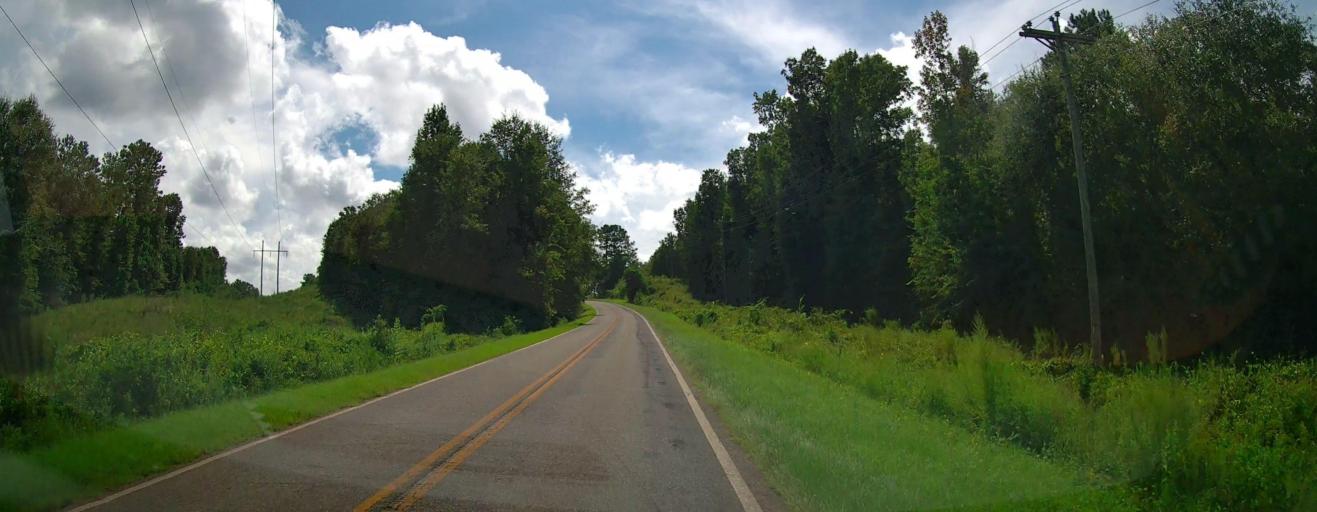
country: US
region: Georgia
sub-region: Macon County
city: Marshallville
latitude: 32.4770
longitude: -83.8660
